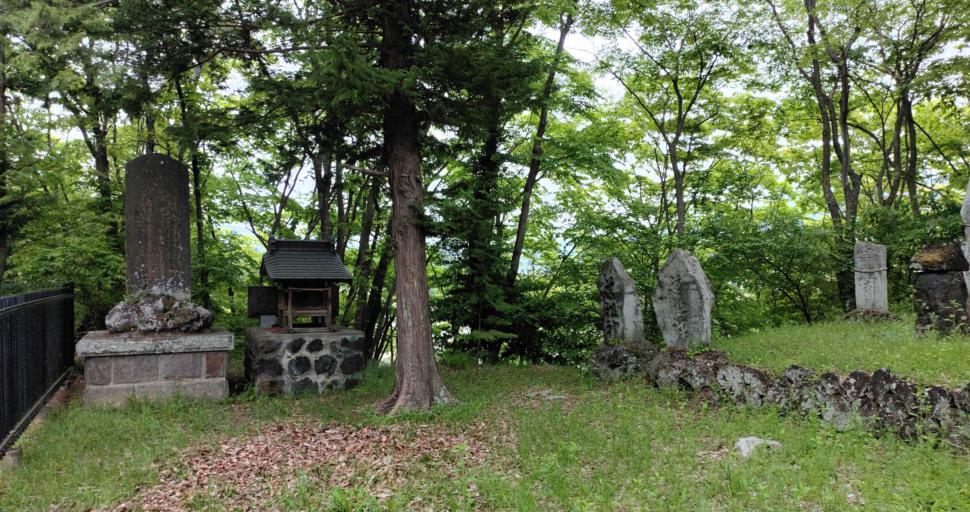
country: JP
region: Nagano
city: Saku
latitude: 36.2746
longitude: 138.4828
